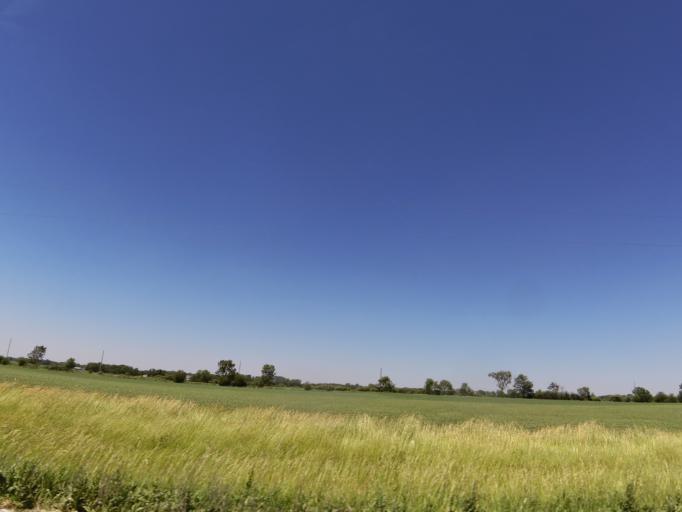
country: US
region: Illinois
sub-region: Livingston County
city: Fairbury
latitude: 40.7447
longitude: -88.4639
